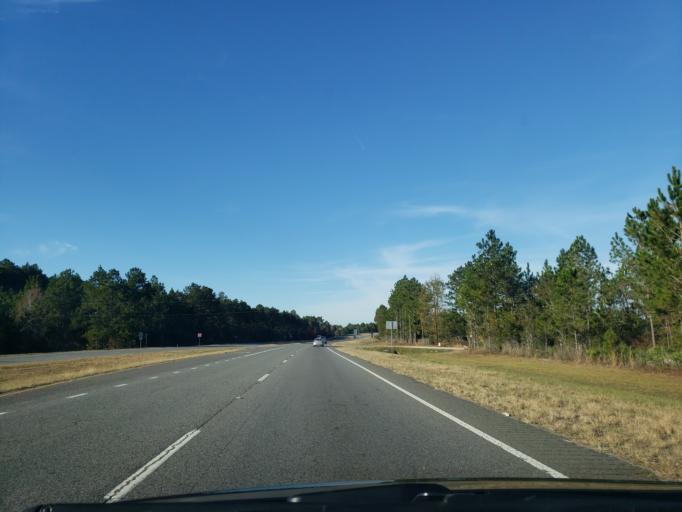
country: US
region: Georgia
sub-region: Ware County
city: Deenwood
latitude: 31.2272
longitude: -82.4258
